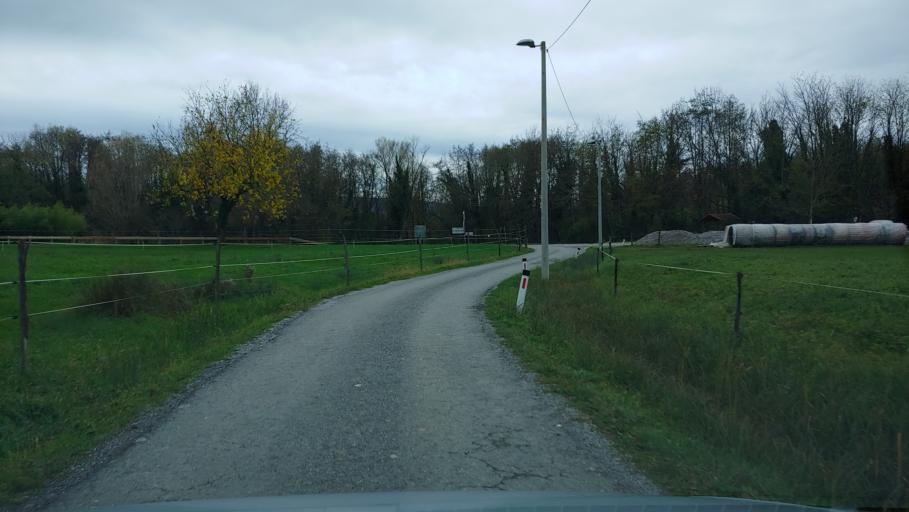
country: SI
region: Sempeter-Vrtojba
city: Sempeter pri Gorici
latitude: 45.9189
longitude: 13.6478
